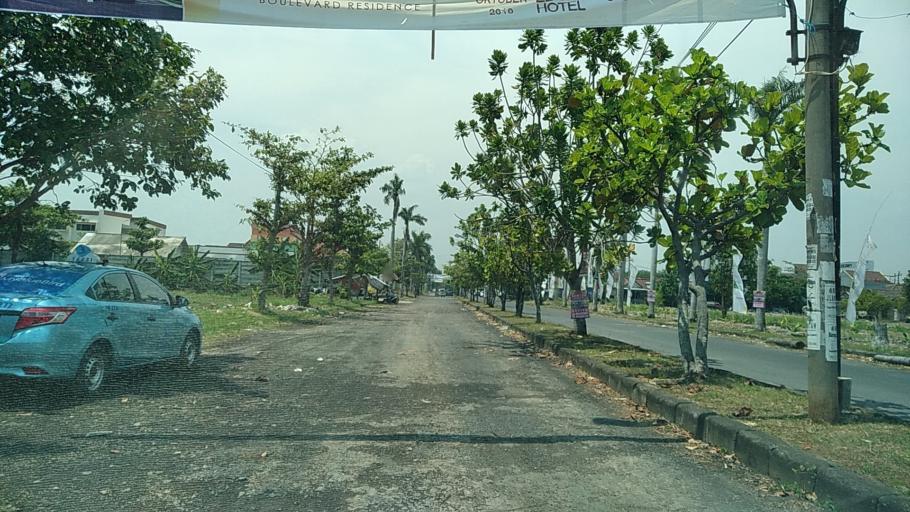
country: ID
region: Central Java
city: Mranggen
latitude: -7.0084
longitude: 110.4847
